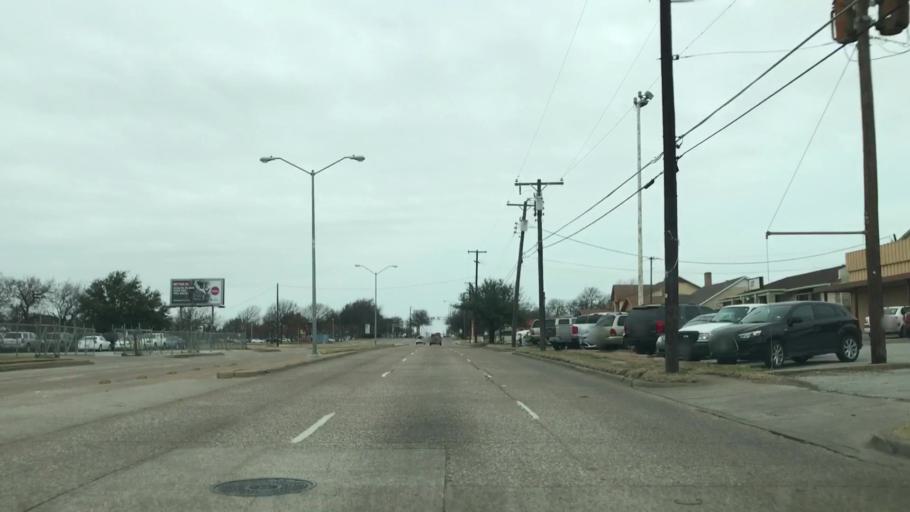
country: US
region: Texas
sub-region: Dallas County
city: Cockrell Hill
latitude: 32.7204
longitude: -96.8666
